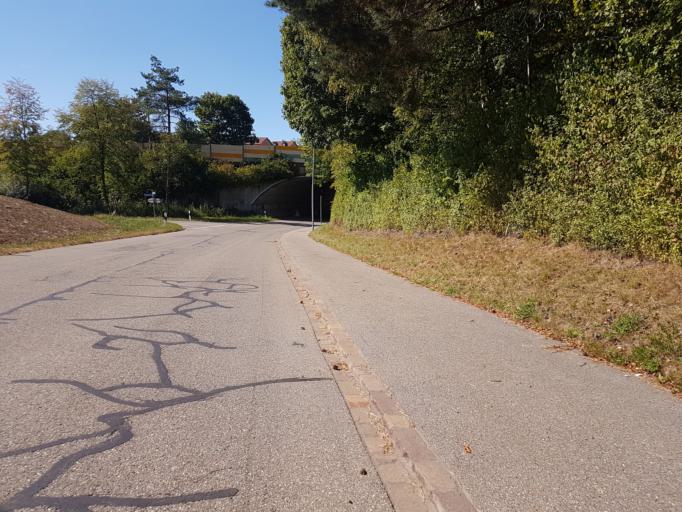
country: CH
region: Zurich
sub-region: Bezirk Pfaeffikon
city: Tagelswangen
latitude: 47.4247
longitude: 8.6763
